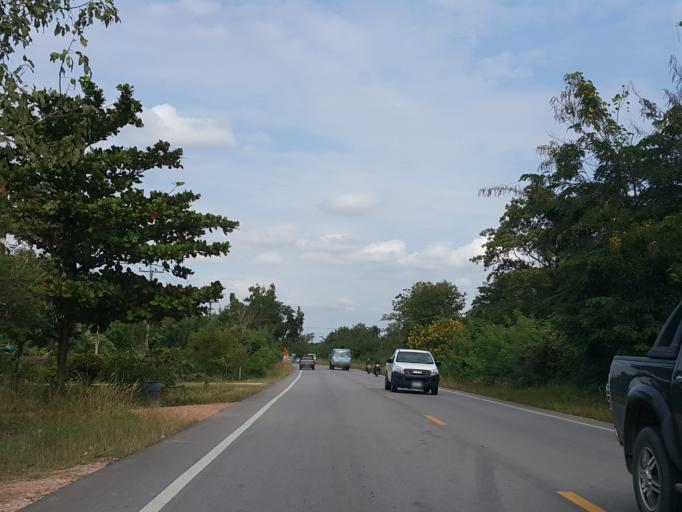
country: TH
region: Lampang
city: Lampang
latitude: 18.3245
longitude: 99.4655
